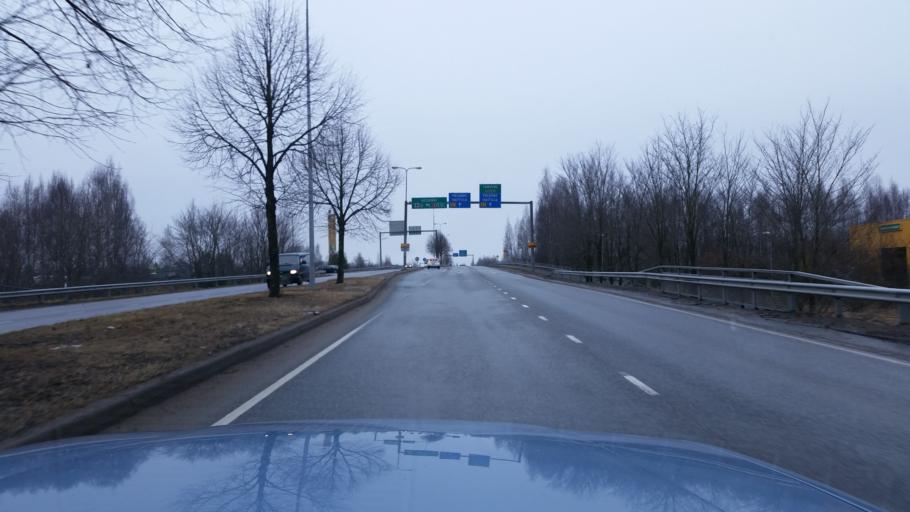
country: FI
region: Haeme
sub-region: Haemeenlinna
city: Haemeenlinna
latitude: 61.0099
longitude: 24.4174
